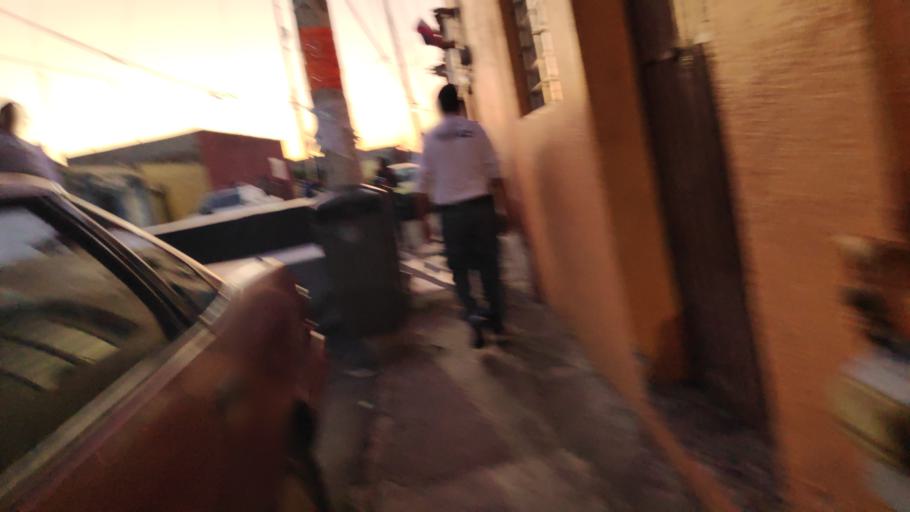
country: MX
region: Queretaro
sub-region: Queretaro
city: Santiago de Queretaro
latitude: 20.5889
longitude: -100.3784
